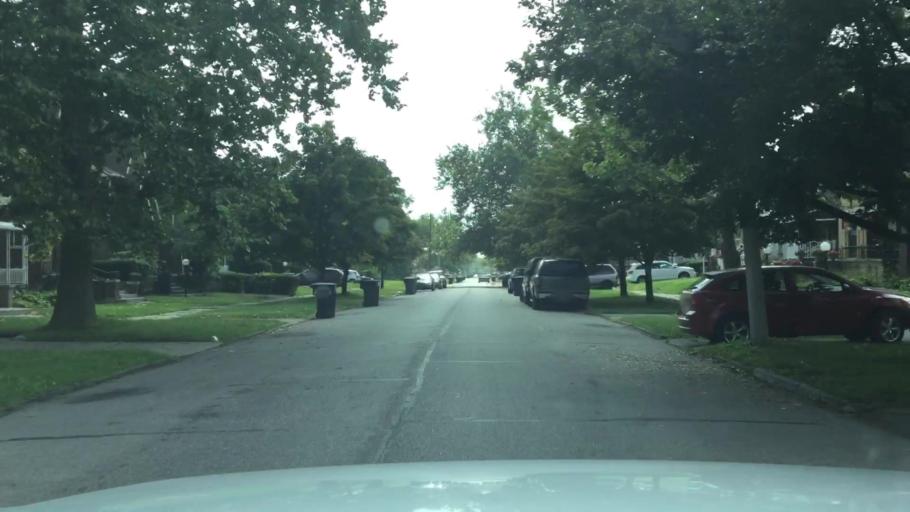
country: US
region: Michigan
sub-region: Wayne County
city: Highland Park
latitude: 42.3913
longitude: -83.1531
